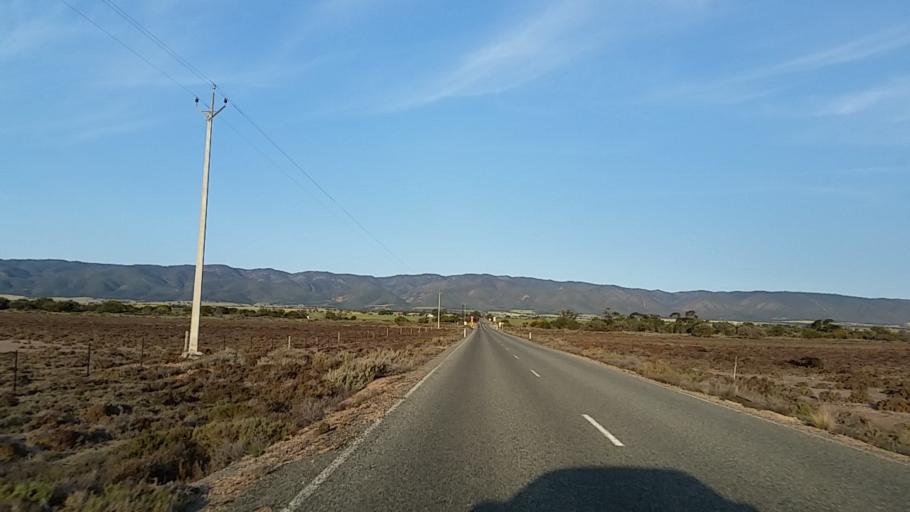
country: AU
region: South Australia
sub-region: Port Pirie City and Dists
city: Port Pirie
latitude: -33.1040
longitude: 138.0517
